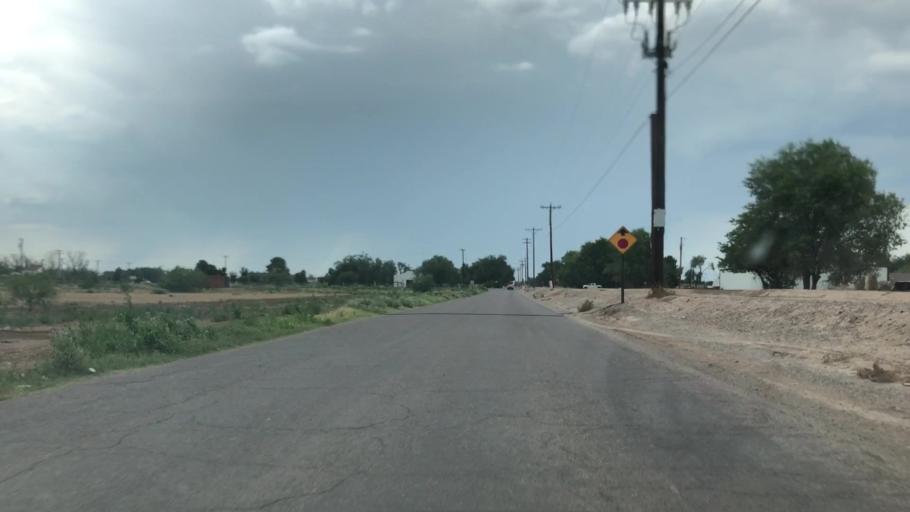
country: US
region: Texas
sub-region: El Paso County
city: Canutillo
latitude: 31.9163
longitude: -106.6248
